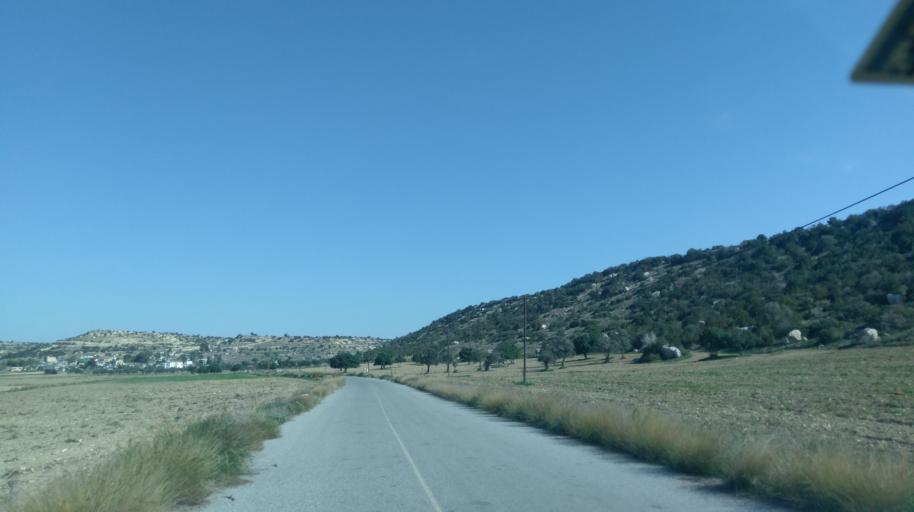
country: CY
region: Ammochostos
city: Trikomo
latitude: 35.3345
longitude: 33.9938
